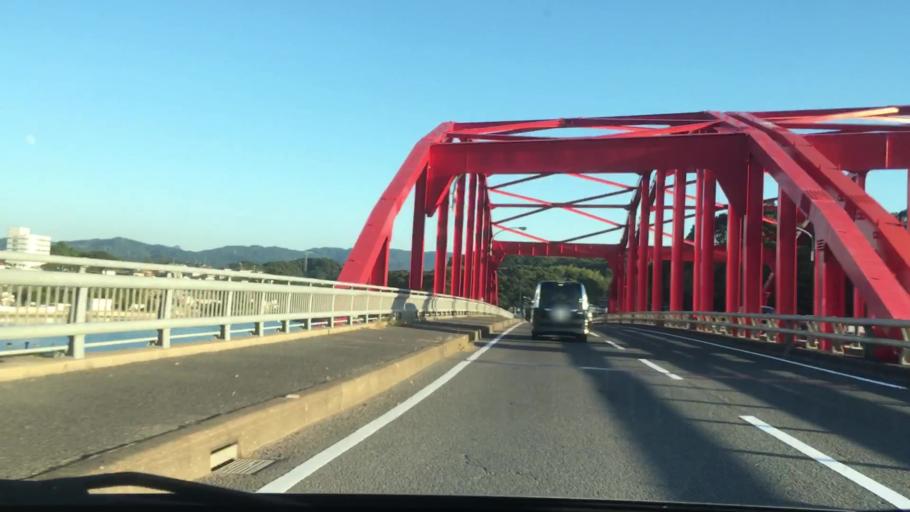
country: JP
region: Nagasaki
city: Sasebo
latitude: 33.1426
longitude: 129.7813
